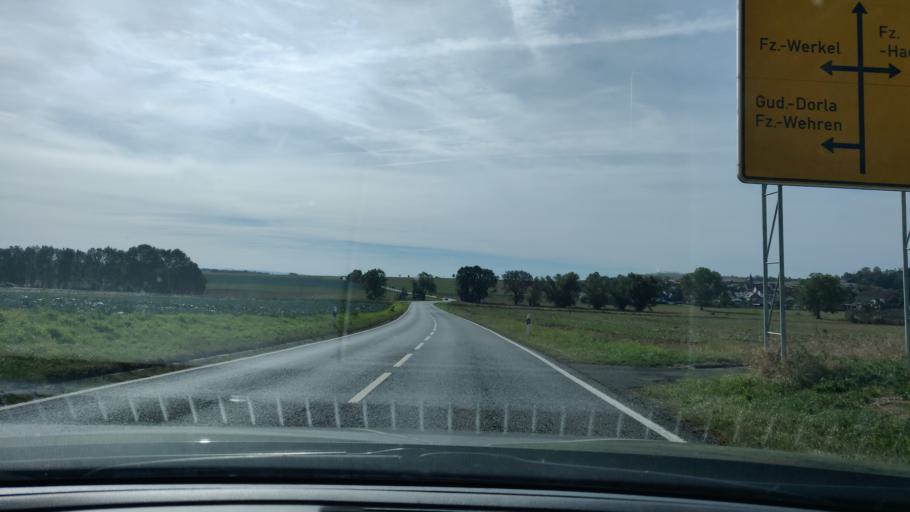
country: DE
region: Hesse
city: Fritzlar
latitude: 51.1673
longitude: 9.2700
